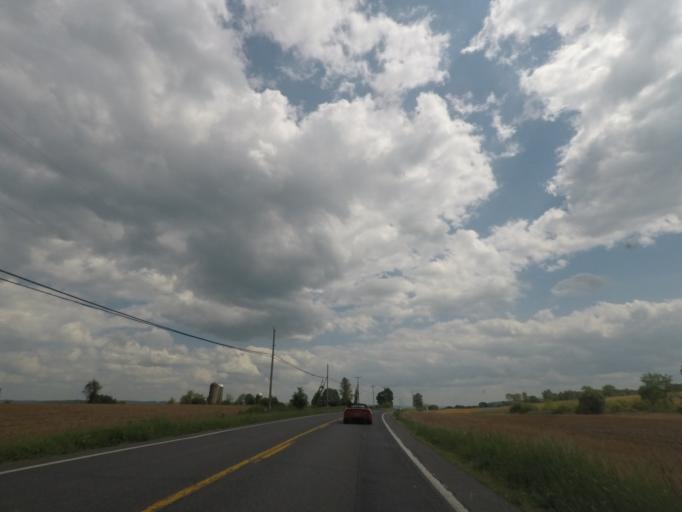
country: US
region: New York
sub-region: Dutchess County
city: Pine Plains
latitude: 41.8956
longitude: -73.5323
